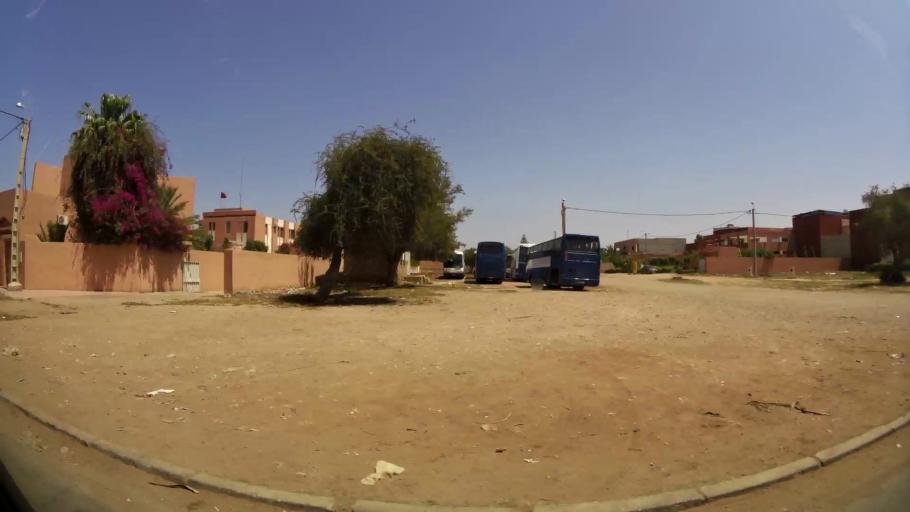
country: MA
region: Souss-Massa-Draa
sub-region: Inezgane-Ait Mellou
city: Inezgane
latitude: 30.3310
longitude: -9.4919
